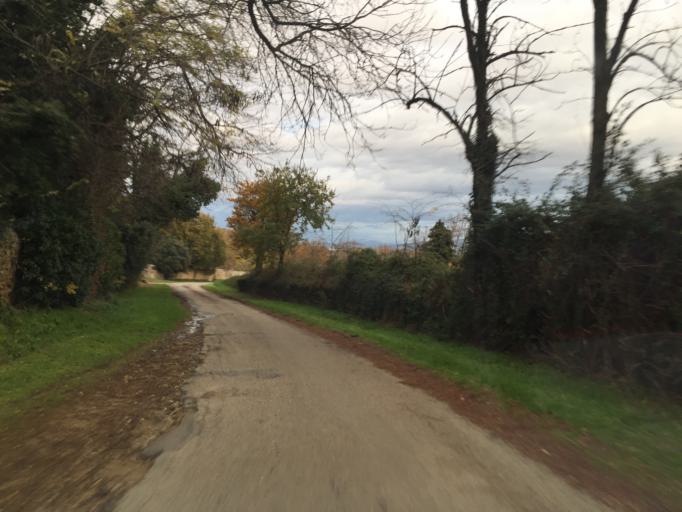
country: FR
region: Provence-Alpes-Cote d'Azur
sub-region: Departement du Vaucluse
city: Courthezon
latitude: 44.0839
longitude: 4.8571
